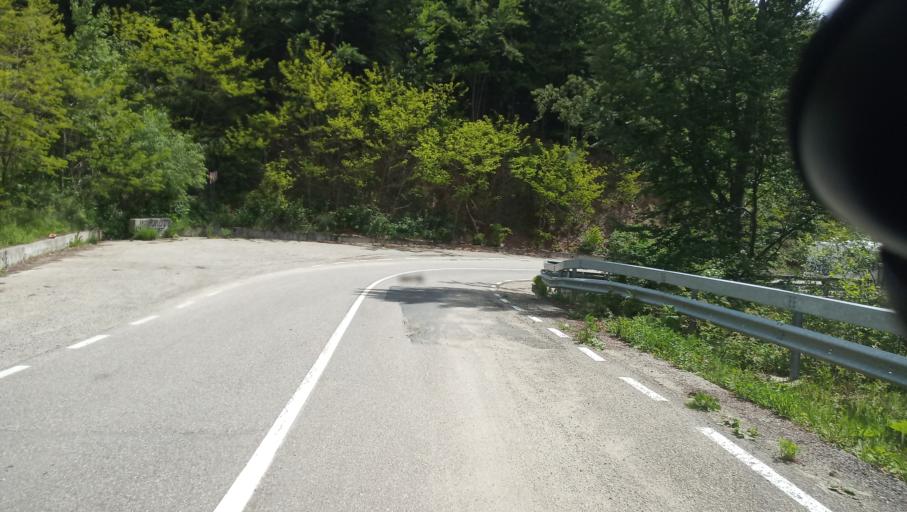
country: RO
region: Caras-Severin
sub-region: Comuna Brebu Nou
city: Brebu Nou
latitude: 45.2511
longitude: 22.1604
